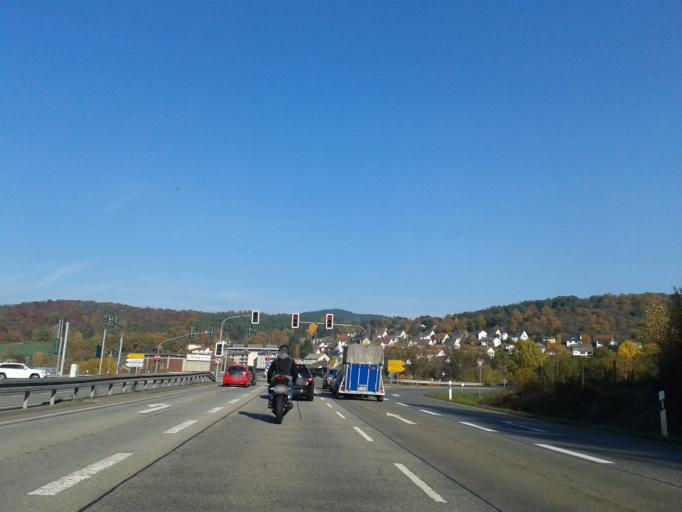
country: DE
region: Hesse
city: Herborn
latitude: 50.6979
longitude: 8.3097
